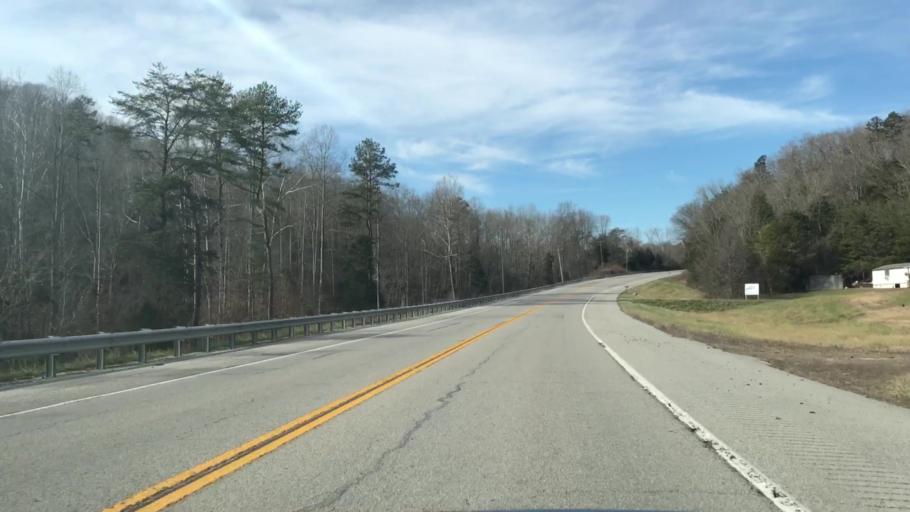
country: US
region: Kentucky
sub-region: Pulaski County
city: Somerset
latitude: 36.9396
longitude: -84.5490
